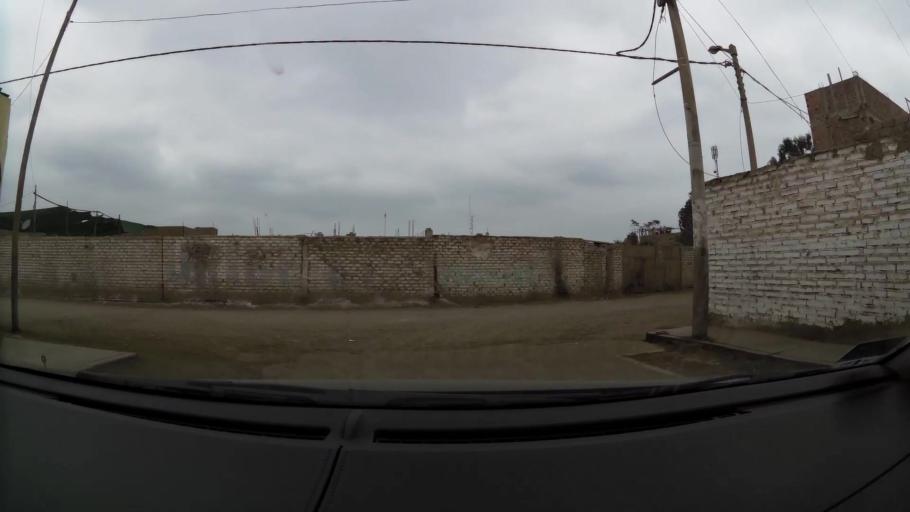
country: PE
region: Lima
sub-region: Provincia de Huaral
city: Huaral
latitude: -11.4987
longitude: -77.2019
